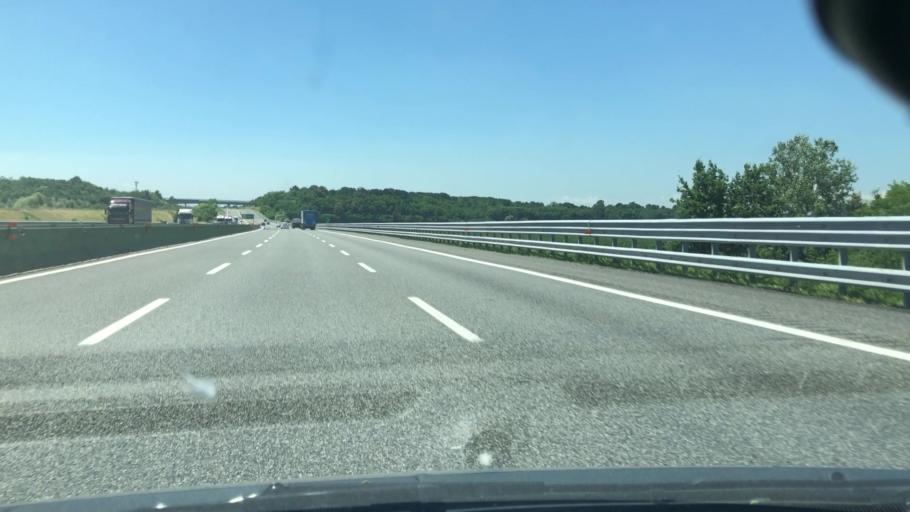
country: IT
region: Piedmont
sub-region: Provincia di Vercelli
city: Carisio
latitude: 45.4236
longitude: 8.1876
